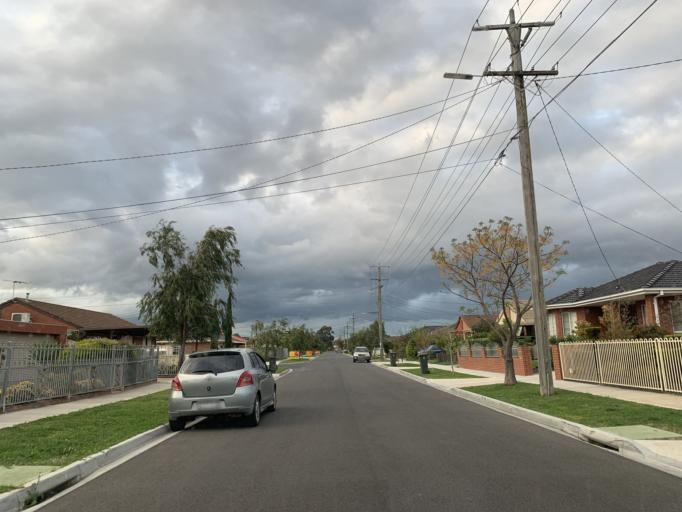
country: AU
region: Victoria
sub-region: Brimbank
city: Kealba
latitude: -37.7506
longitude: 144.8240
